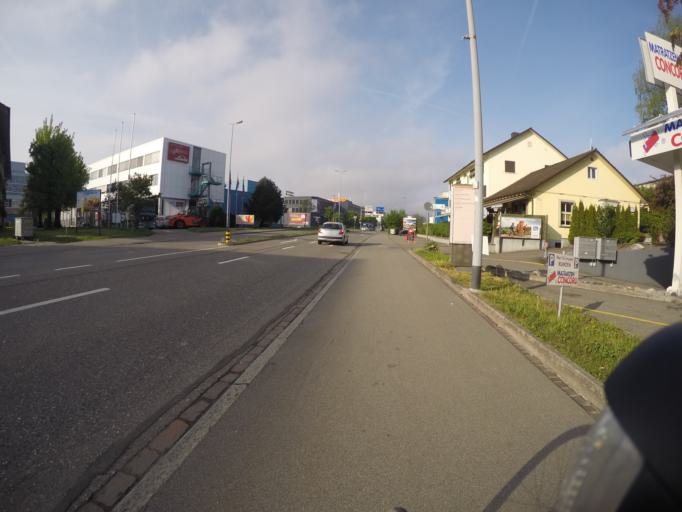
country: CH
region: Zurich
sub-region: Bezirk Buelach
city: Dietlikon / Dietlikon (Dorf)
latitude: 47.4149
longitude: 8.6197
